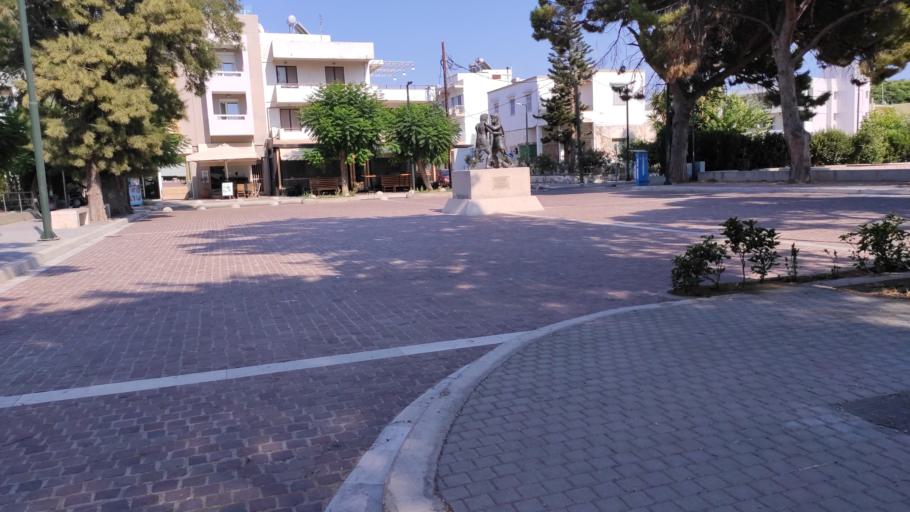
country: GR
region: South Aegean
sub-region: Nomos Dodekanisou
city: Kos
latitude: 36.8916
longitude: 27.2898
